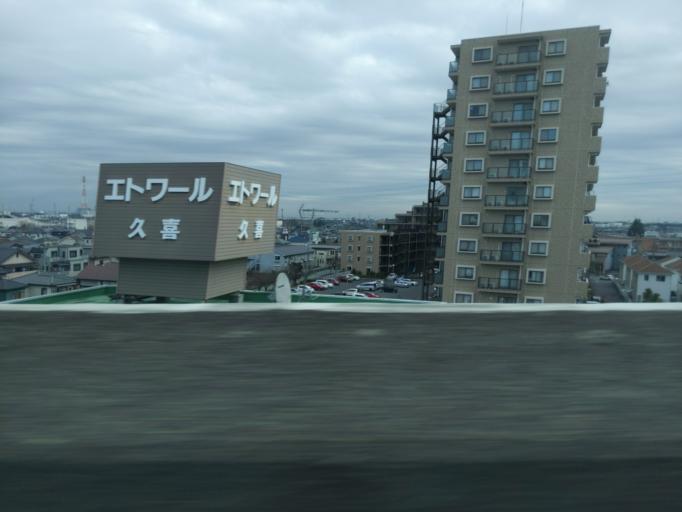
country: JP
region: Saitama
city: Kukichuo
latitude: 36.0712
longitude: 139.6810
